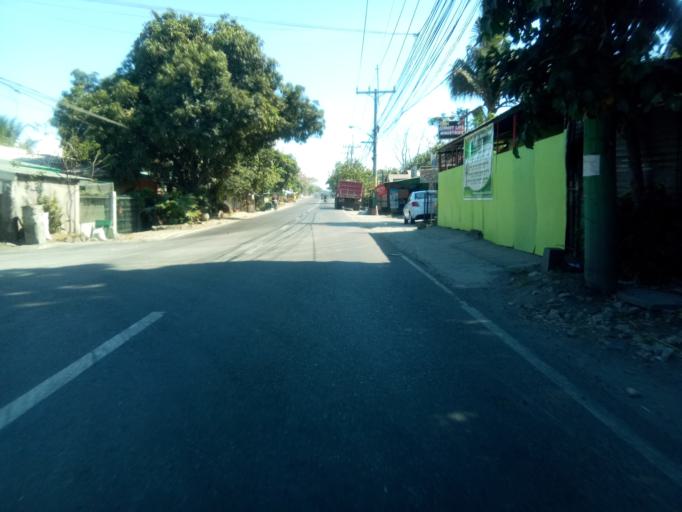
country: PH
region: Calabarzon
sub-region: Province of Cavite
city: Bulihan
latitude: 14.2953
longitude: 120.9904
